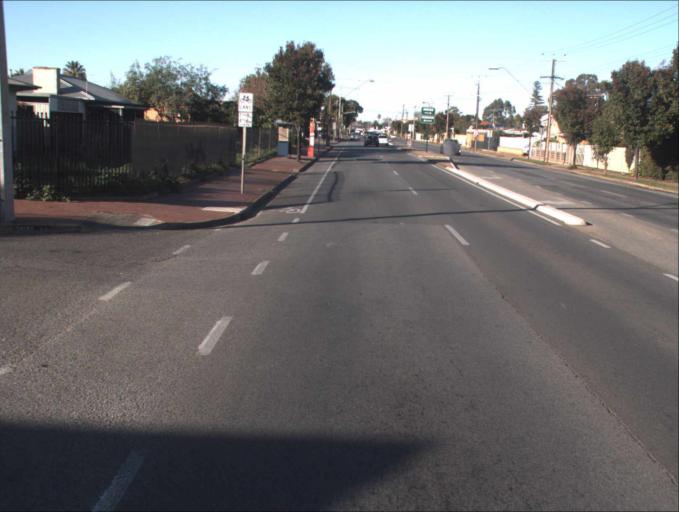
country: AU
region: South Australia
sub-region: Charles Sturt
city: Woodville North
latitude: -34.8704
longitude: 138.5481
